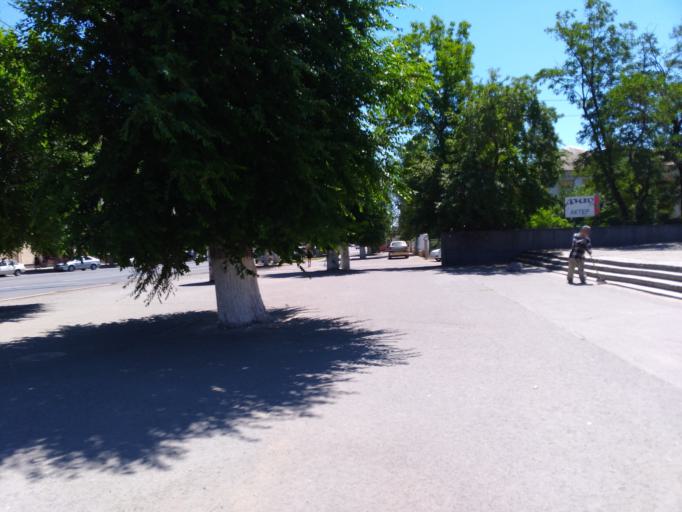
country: RU
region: Volgograd
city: Volgograd
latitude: 48.7071
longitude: 44.5069
